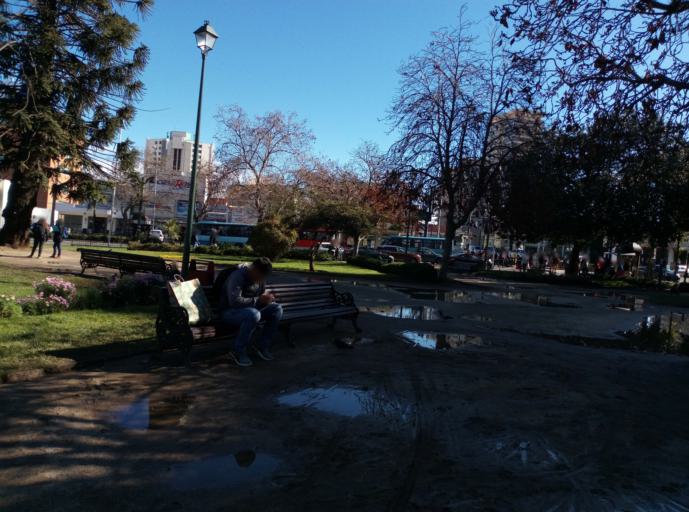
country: CL
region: Valparaiso
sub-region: Provincia de Valparaiso
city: Vina del Mar
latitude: -33.0096
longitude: -71.5482
